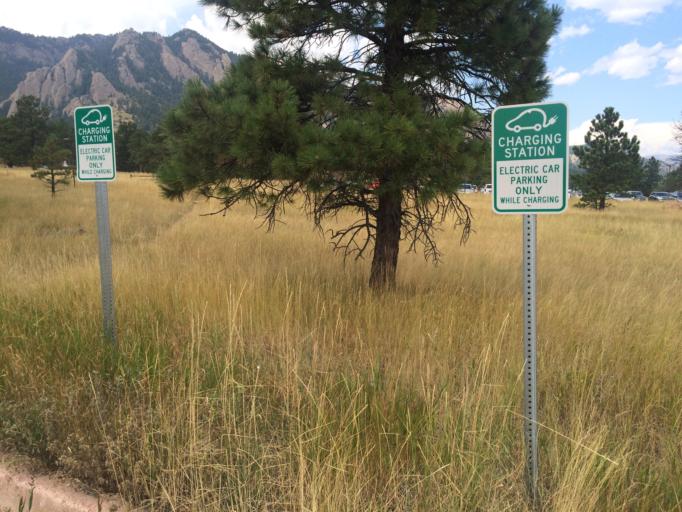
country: US
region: Colorado
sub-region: Boulder County
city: Boulder
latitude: 39.9789
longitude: -105.2736
